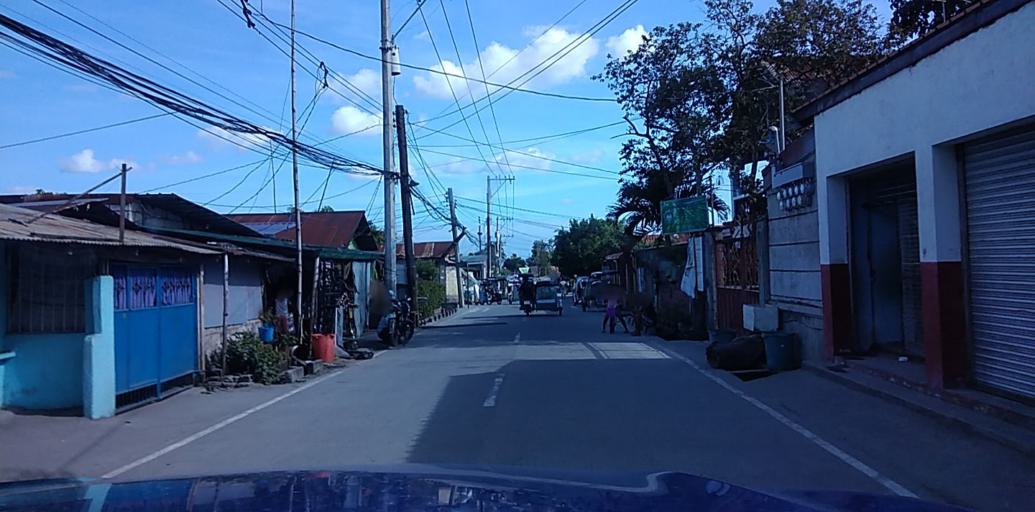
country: PH
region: Central Luzon
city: Santol
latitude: 15.1474
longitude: 120.5475
